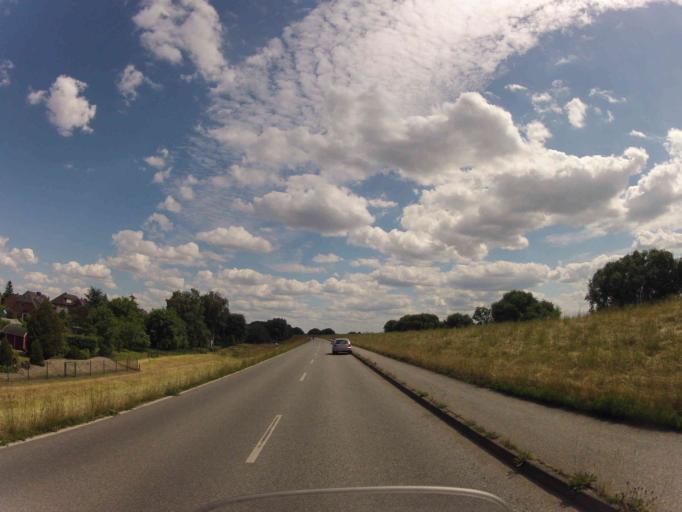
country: DE
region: Lower Saxony
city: Stelle
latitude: 53.4049
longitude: 10.1603
